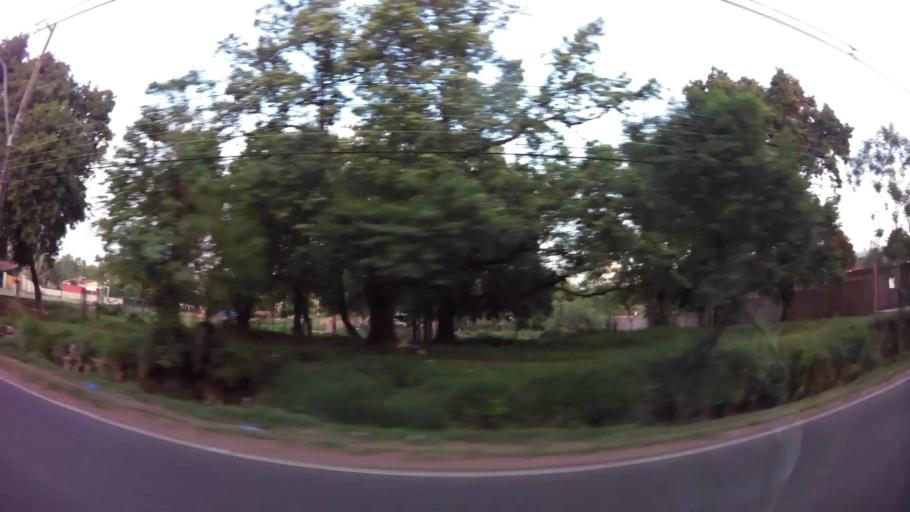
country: PY
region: Central
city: San Lorenzo
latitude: -25.3727
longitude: -57.4919
